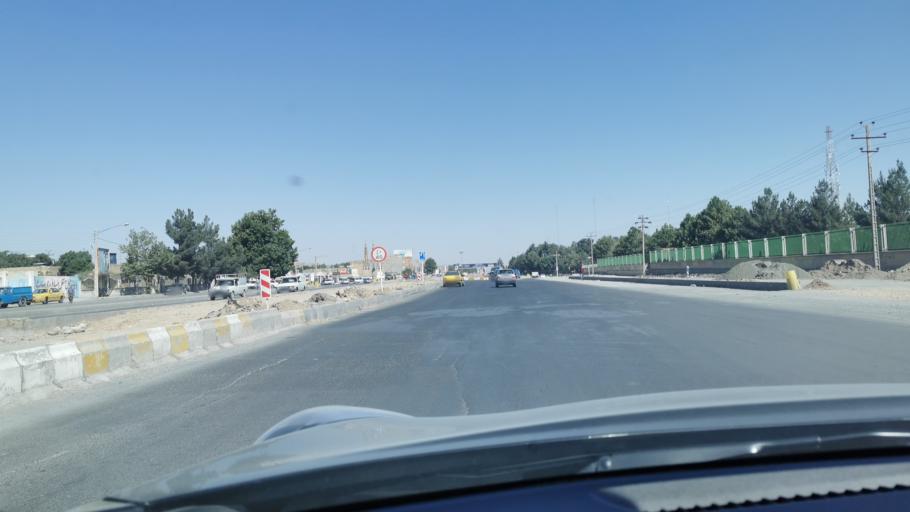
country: IR
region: Razavi Khorasan
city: Chenaran
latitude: 36.6393
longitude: 59.1209
